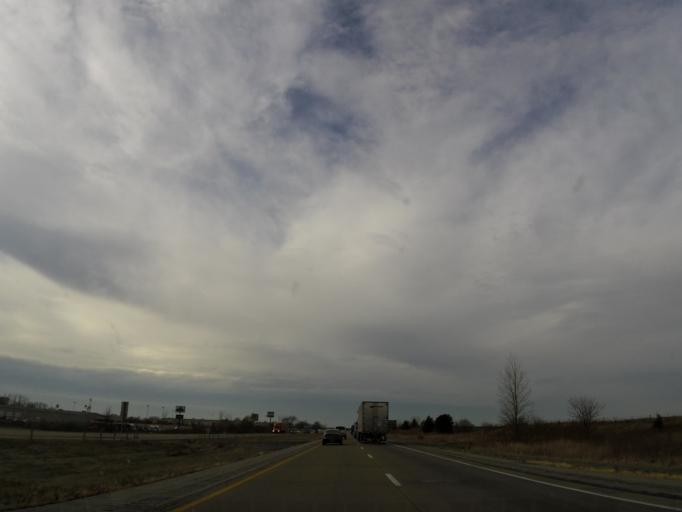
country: US
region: Iowa
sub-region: Scott County
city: Eldridge
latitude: 41.5999
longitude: -90.6056
